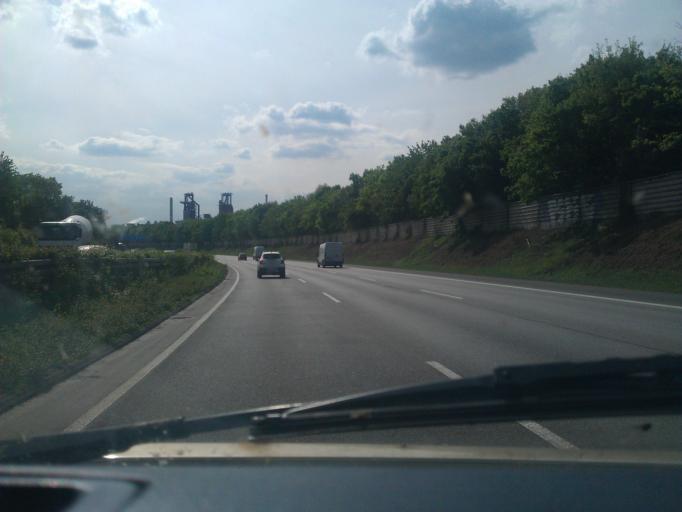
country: DE
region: North Rhine-Westphalia
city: Meiderich
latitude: 51.4874
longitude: 6.7506
